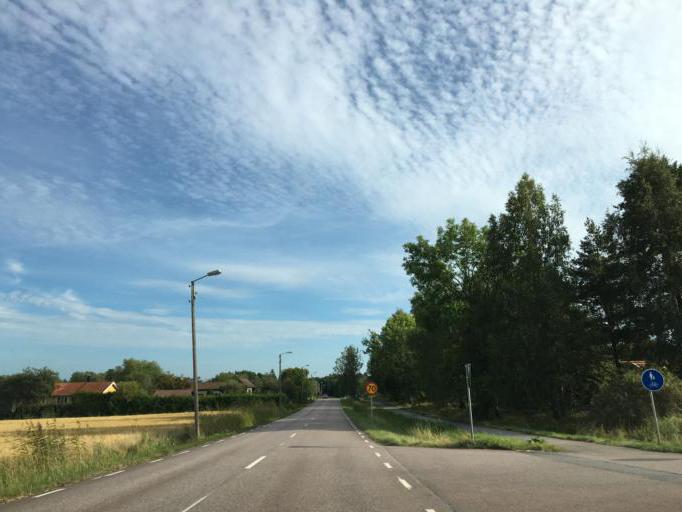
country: SE
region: Soedermanland
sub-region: Eskilstuna Kommun
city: Torshalla
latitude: 59.4463
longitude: 16.4492
